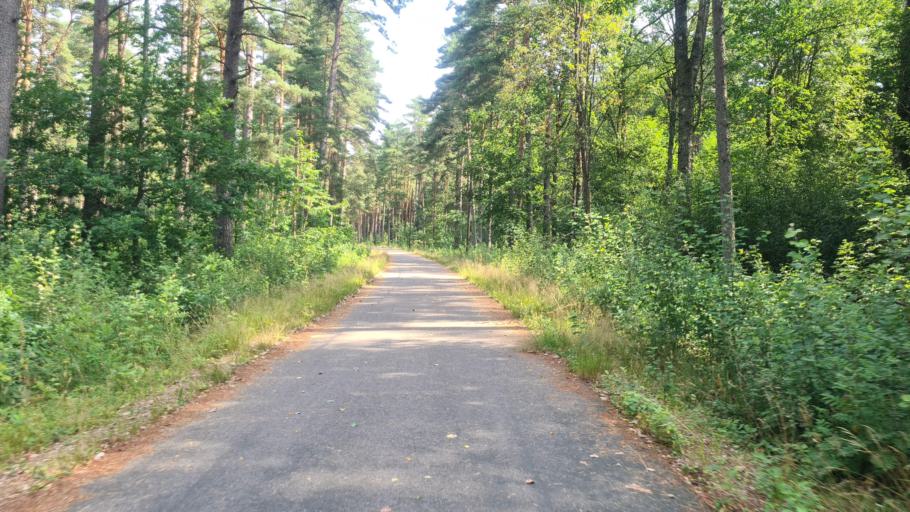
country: SE
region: Kronoberg
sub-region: Ljungby Kommun
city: Ljungby
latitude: 56.8435
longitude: 13.9613
